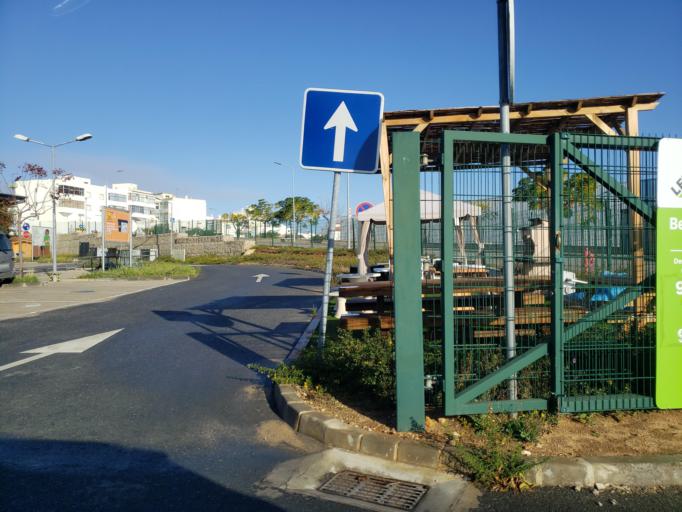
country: PT
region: Faro
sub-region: Portimao
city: Portimao
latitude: 37.1481
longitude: -8.5501
